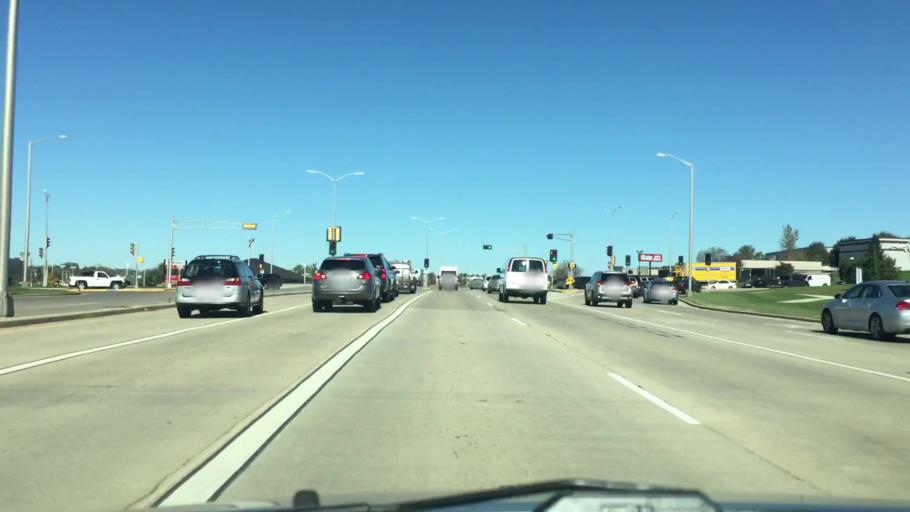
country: US
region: Wisconsin
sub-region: Waukesha County
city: Waukesha
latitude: 43.0200
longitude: -88.2011
